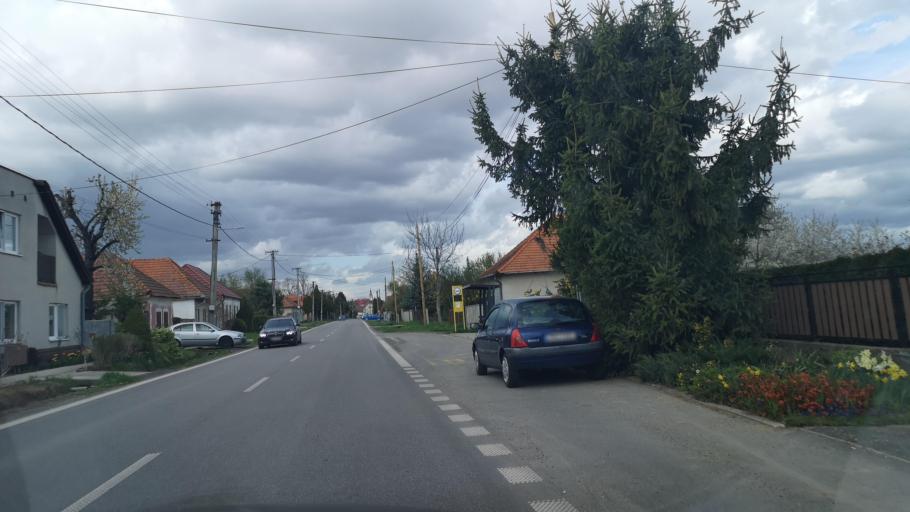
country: SK
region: Nitriansky
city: Zlate Moravce
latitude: 48.3305
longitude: 18.3516
